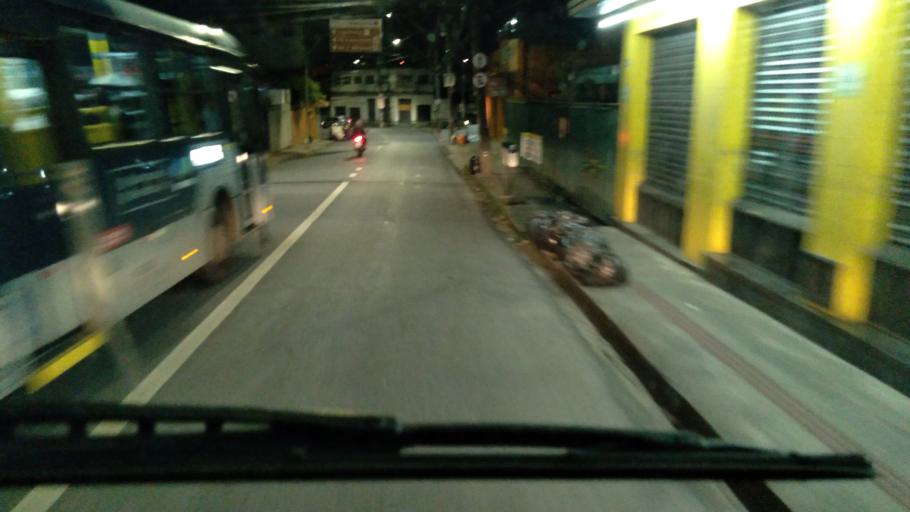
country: BR
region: Minas Gerais
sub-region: Belo Horizonte
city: Belo Horizonte
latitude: -19.9120
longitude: -43.9610
